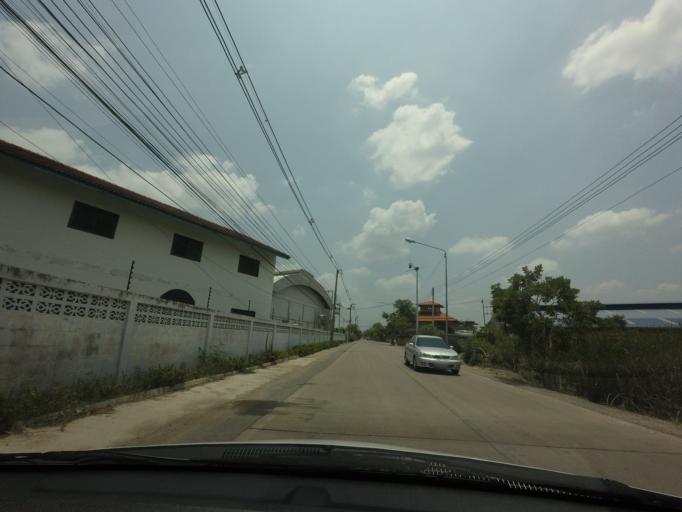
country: TH
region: Pathum Thani
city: Sam Khok
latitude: 14.0433
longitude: 100.5423
